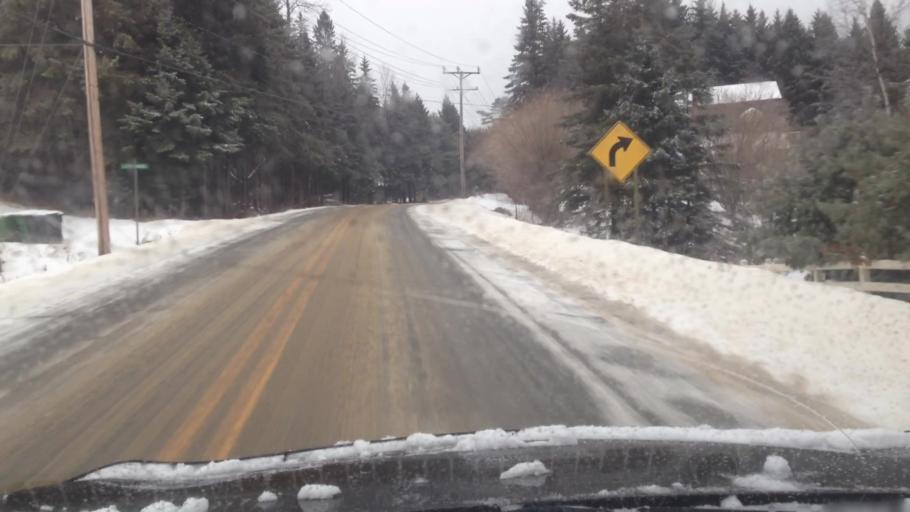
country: CA
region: Quebec
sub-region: Laurentides
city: Mont-Tremblant
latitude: 46.0429
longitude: -74.6072
